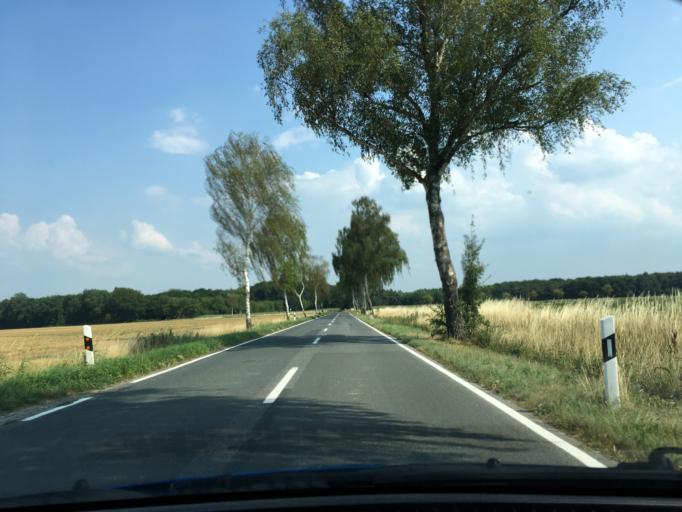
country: DE
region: Lower Saxony
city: Tosterglope
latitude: 53.2328
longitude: 10.8266
